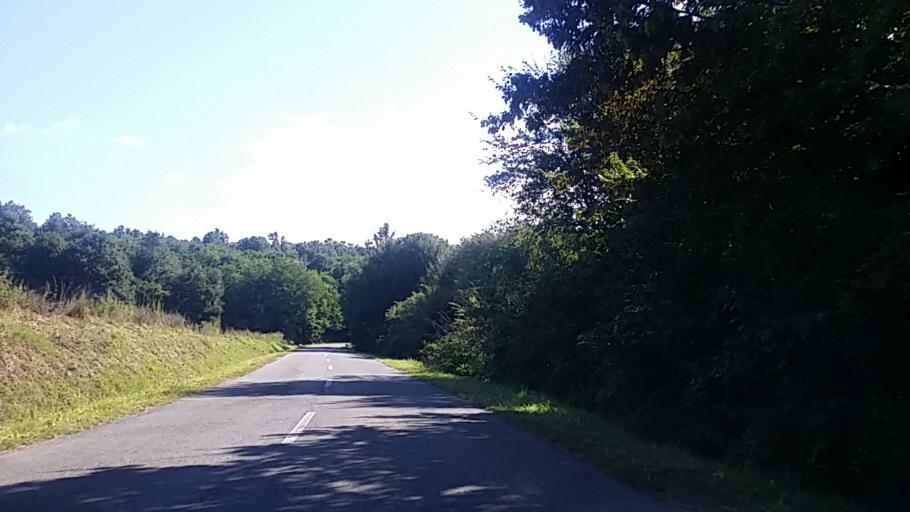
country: HU
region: Baranya
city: Pellerd
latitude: 46.1394
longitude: 18.1352
